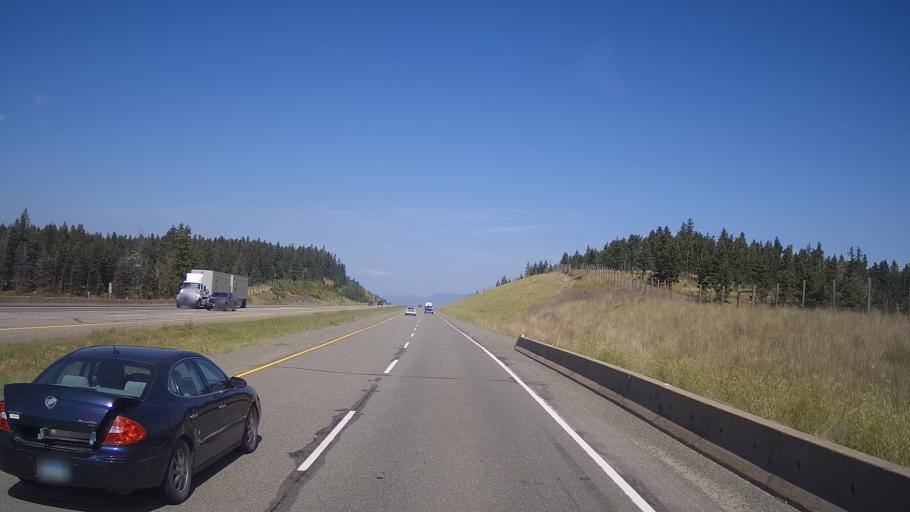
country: CA
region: British Columbia
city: Kamloops
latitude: 50.5790
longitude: -120.4639
